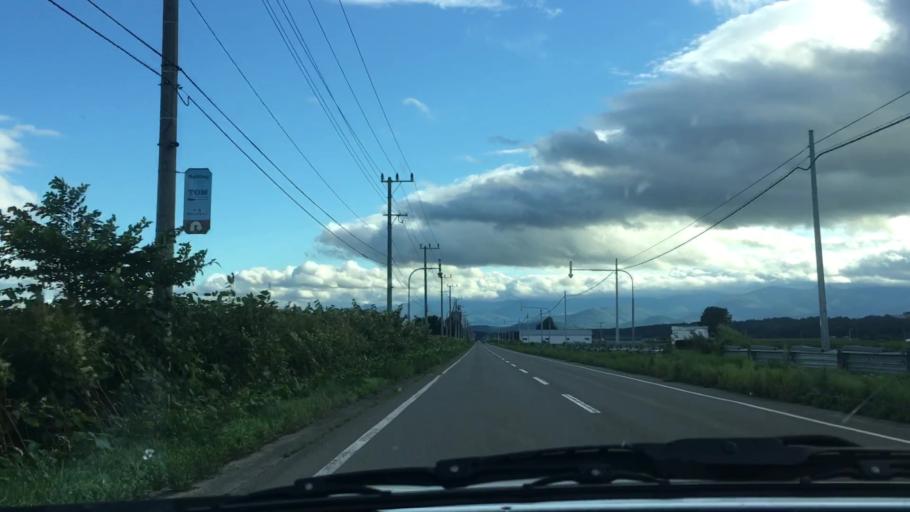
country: JP
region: Hokkaido
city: Otofuke
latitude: 43.1570
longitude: 142.9027
